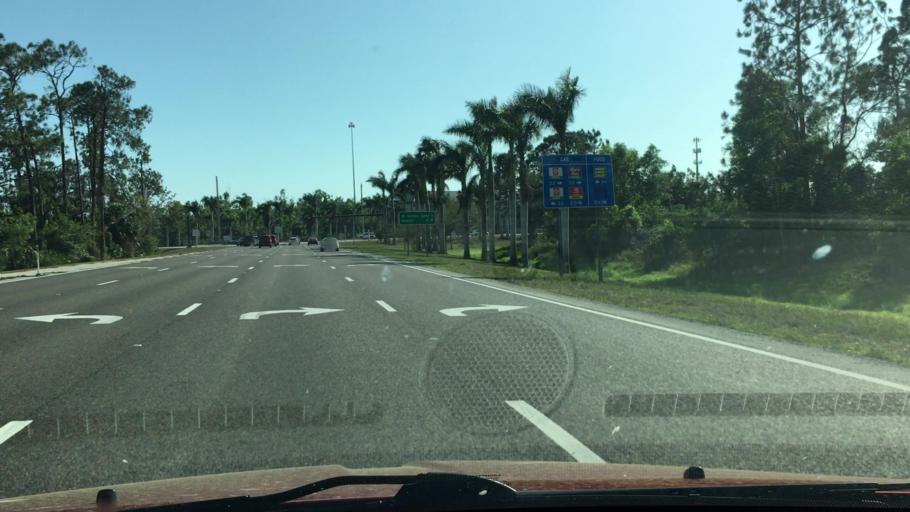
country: US
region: Florida
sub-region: Collier County
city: Vineyards
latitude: 26.2134
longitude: -81.7373
